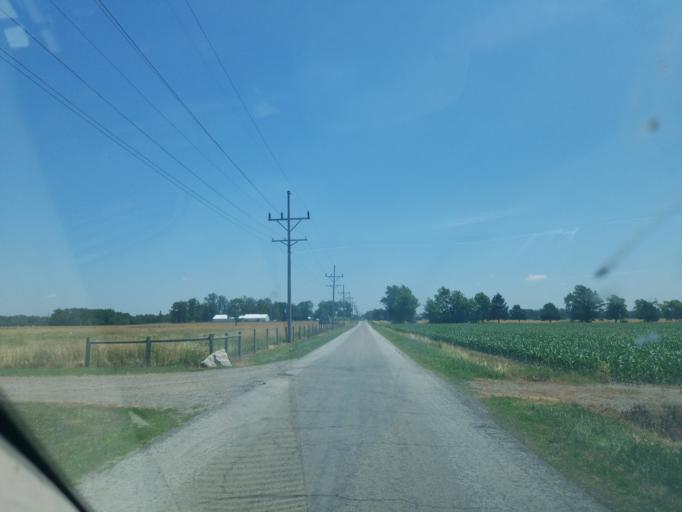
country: US
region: Ohio
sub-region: Allen County
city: Delphos
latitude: 40.7794
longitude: -84.3266
